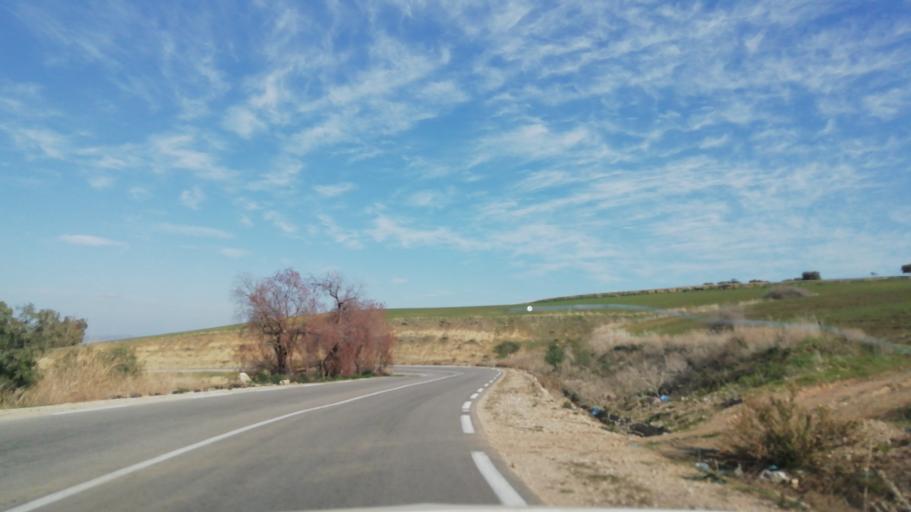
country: DZ
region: Tlemcen
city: Chetouane
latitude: 34.9648
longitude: -1.2472
